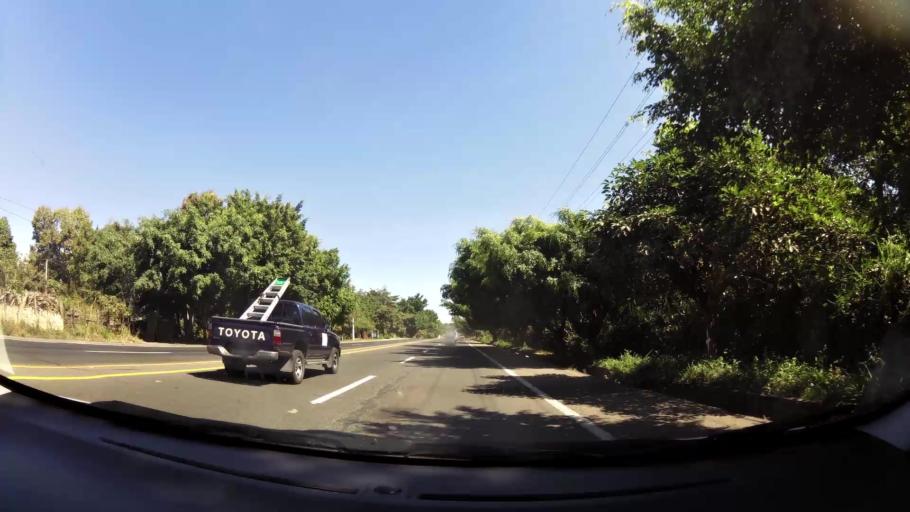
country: SV
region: Santa Ana
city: Chalchuapa
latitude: 13.9733
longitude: -89.7020
